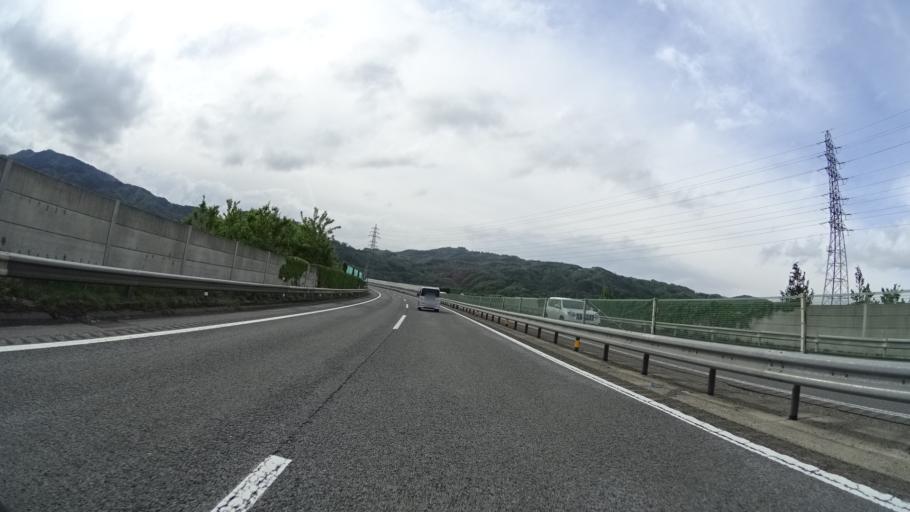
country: JP
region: Nagano
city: Nagano-shi
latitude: 36.5569
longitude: 138.1211
